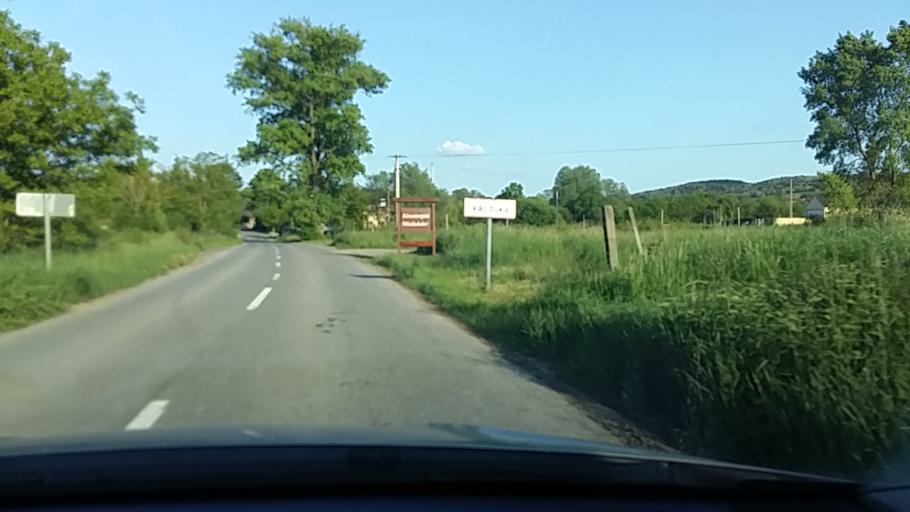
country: HU
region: Pest
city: Szod
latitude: 47.7509
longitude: 19.2060
